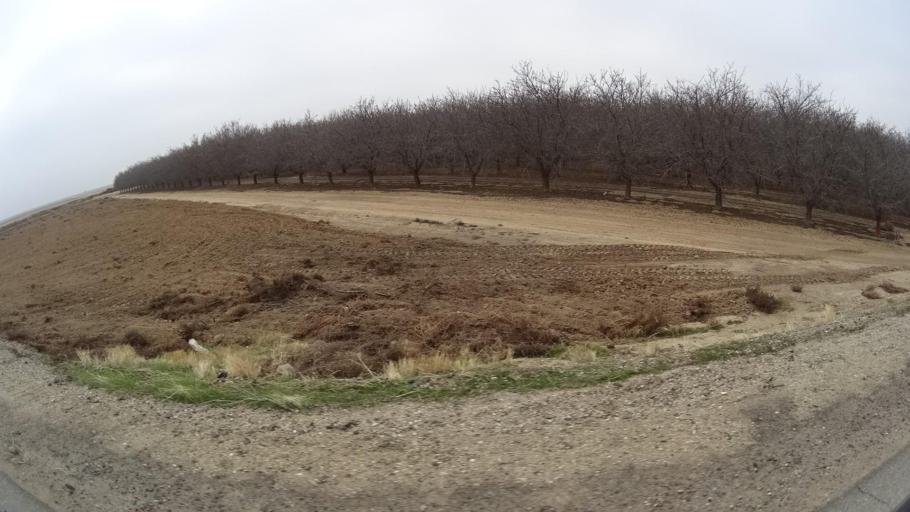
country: US
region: California
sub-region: Kern County
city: Maricopa
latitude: 35.1027
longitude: -119.3408
